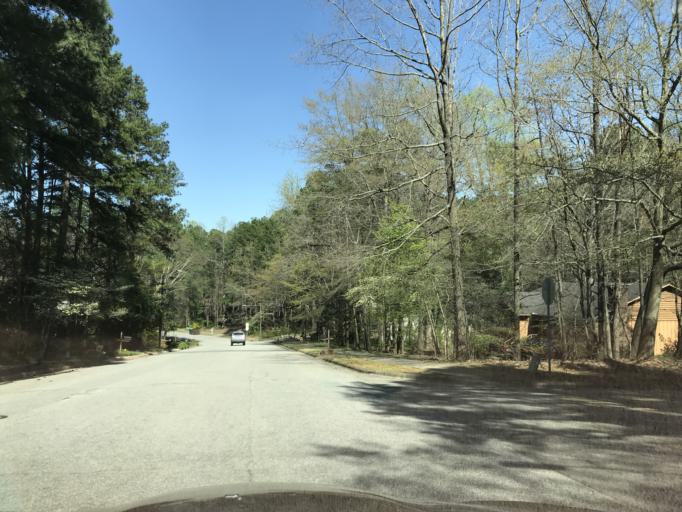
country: US
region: North Carolina
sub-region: Wake County
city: West Raleigh
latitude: 35.7739
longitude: -78.6996
